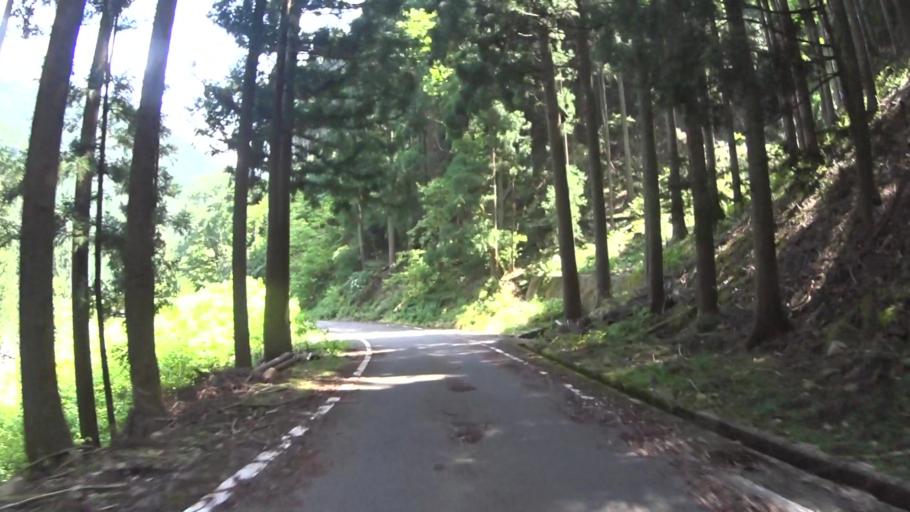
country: JP
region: Kyoto
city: Maizuru
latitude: 35.3496
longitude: 135.5209
